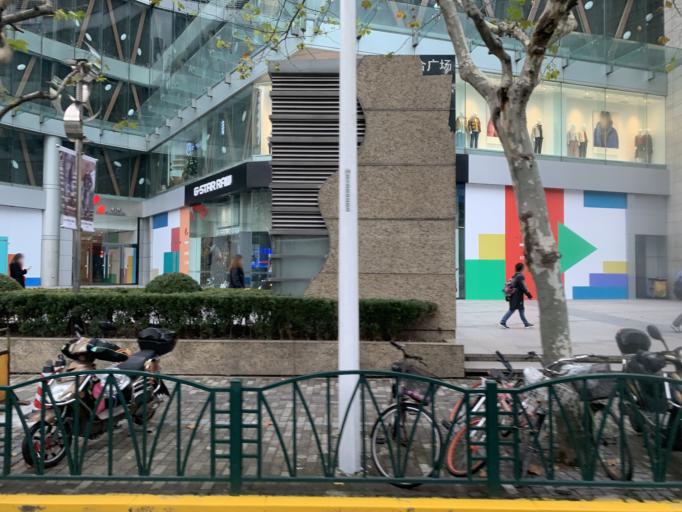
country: CN
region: Shanghai Shi
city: Pudong
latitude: 31.2313
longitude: 121.5116
